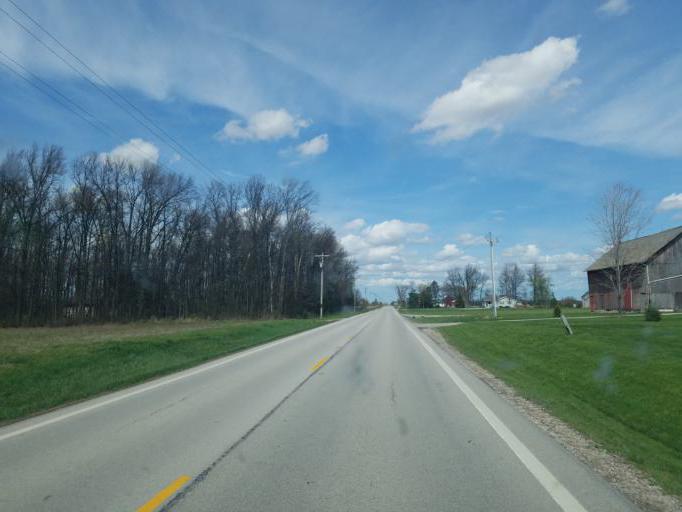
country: US
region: Ohio
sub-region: Huron County
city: Bellevue
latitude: 41.1855
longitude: -82.8313
